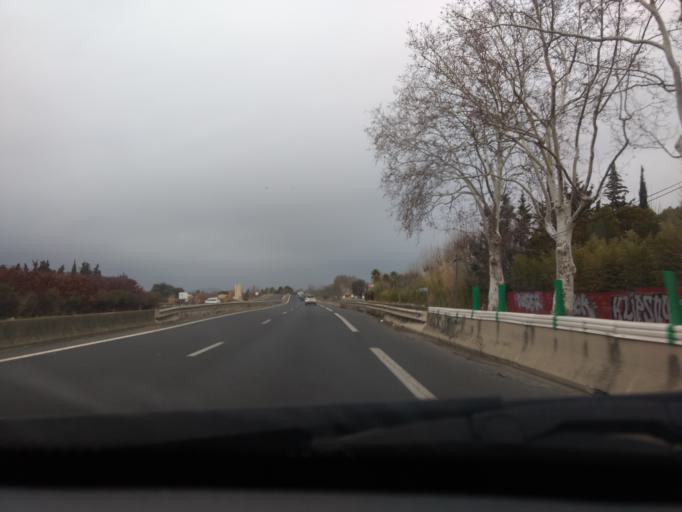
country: FR
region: Languedoc-Roussillon
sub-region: Departement de l'Herault
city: Lattes
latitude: 43.5520
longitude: 3.8934
